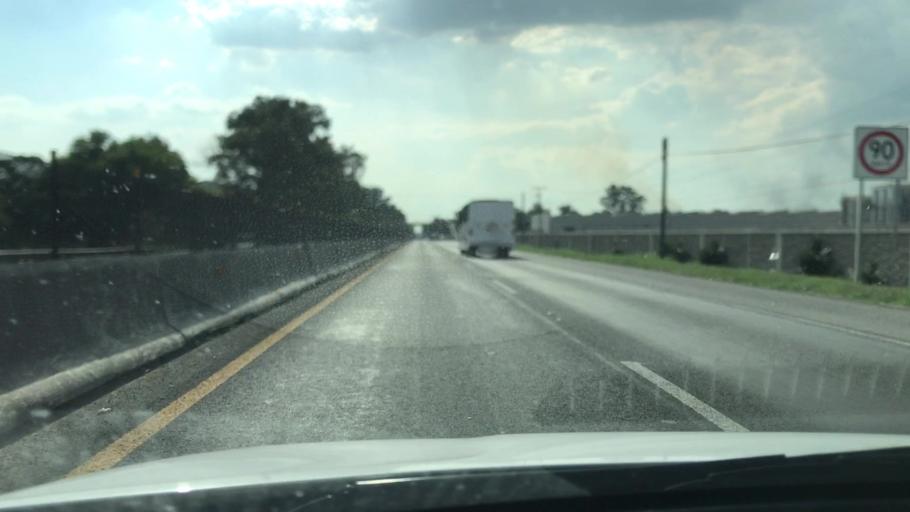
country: MX
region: Guanajuato
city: Valtierrilla
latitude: 20.5512
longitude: -101.1454
